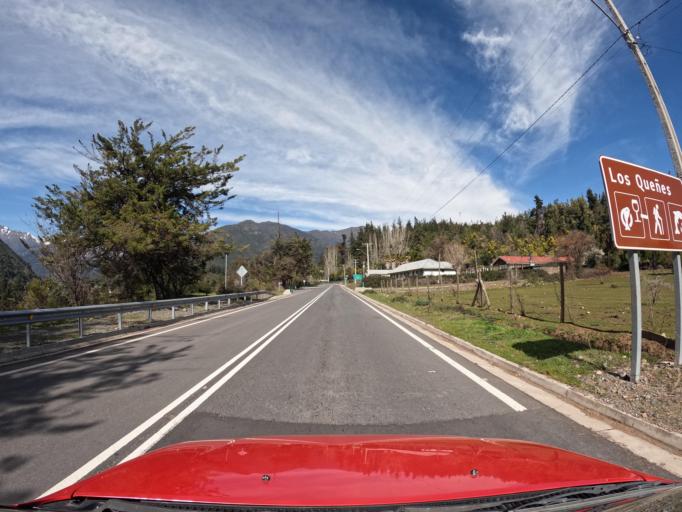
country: CL
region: O'Higgins
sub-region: Provincia de Colchagua
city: Chimbarongo
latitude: -34.9989
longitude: -70.8173
